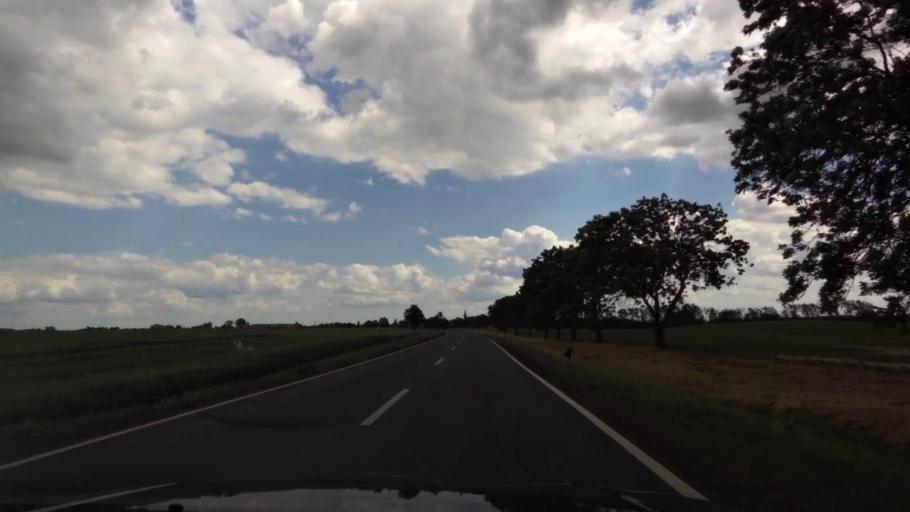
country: PL
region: West Pomeranian Voivodeship
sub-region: Powiat mysliborski
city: Mysliborz
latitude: 52.9552
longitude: 14.7724
